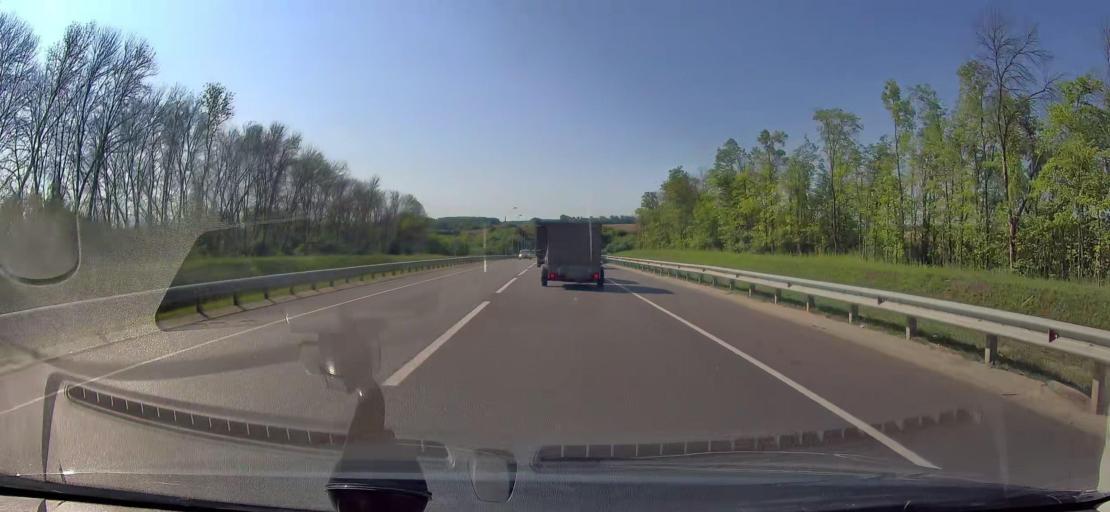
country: RU
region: Orjol
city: Kromy
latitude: 52.6253
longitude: 35.7567
